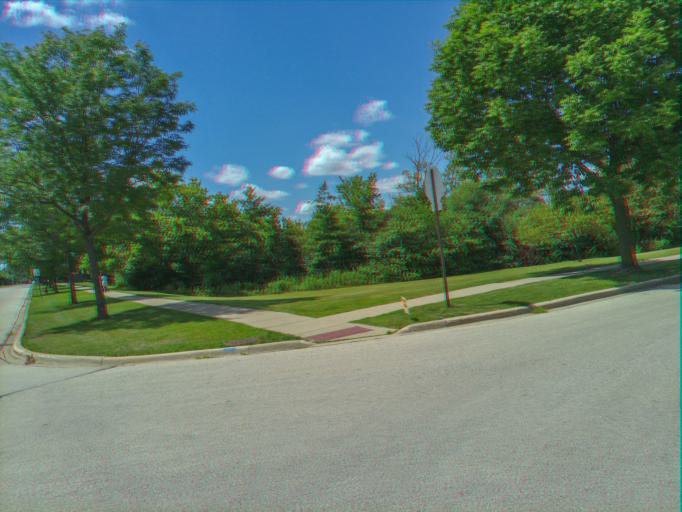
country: US
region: Illinois
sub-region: Lake County
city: Long Grove
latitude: 42.1479
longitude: -87.9996
